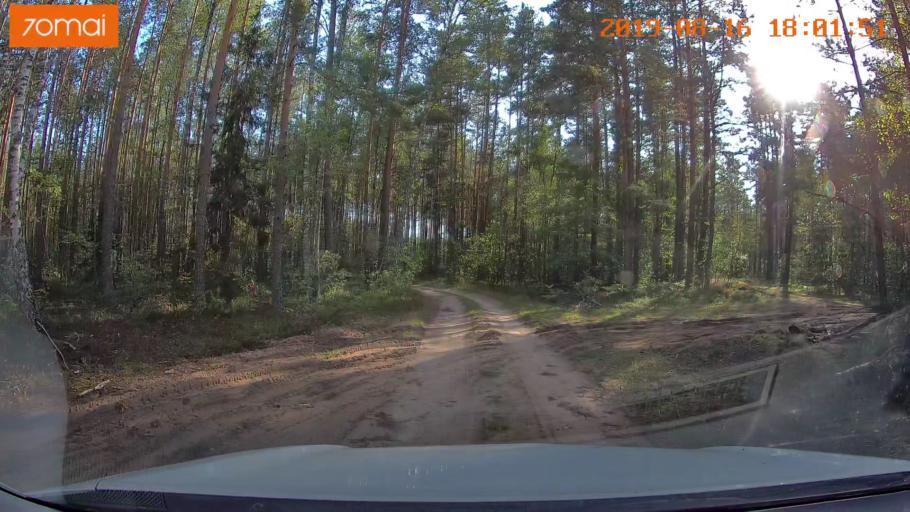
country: BY
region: Mogilev
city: Asipovichy
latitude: 53.2217
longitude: 28.6564
